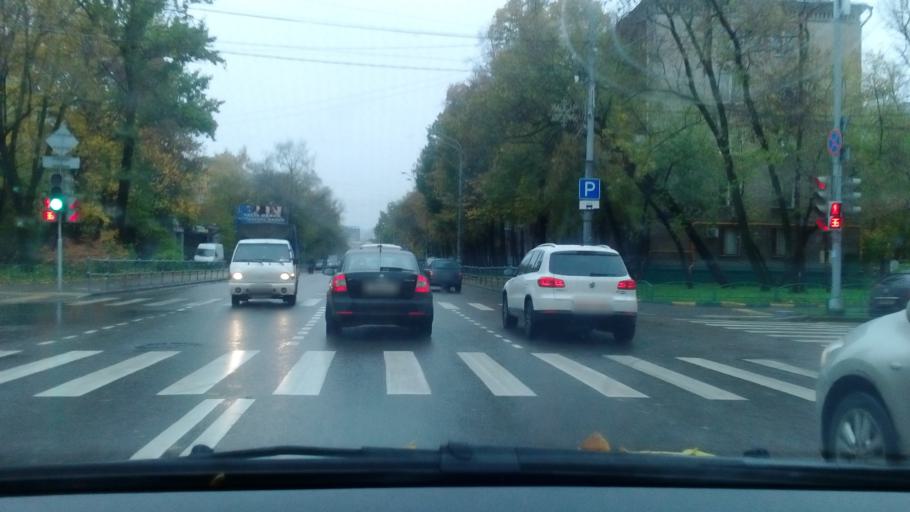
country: RU
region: Moscow
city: Mar'ina Roshcha
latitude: 55.7980
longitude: 37.5761
